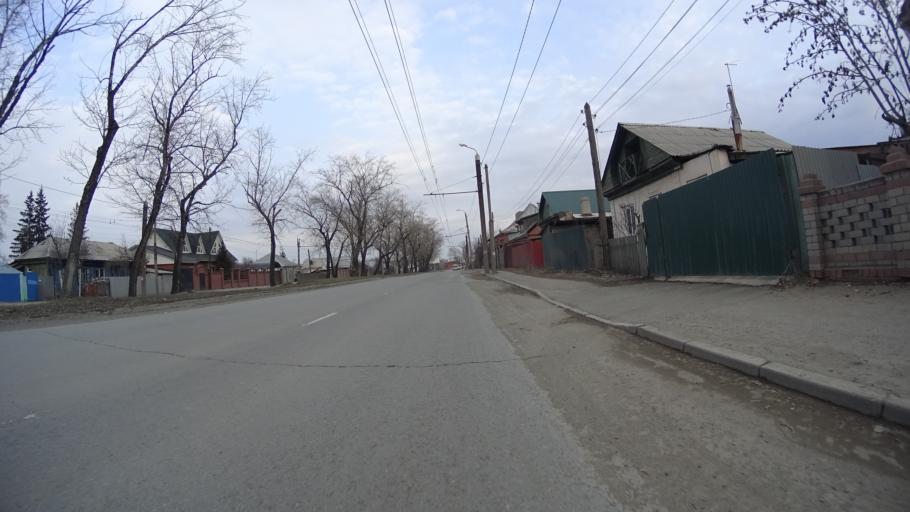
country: RU
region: Chelyabinsk
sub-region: Gorod Chelyabinsk
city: Chelyabinsk
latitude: 55.1913
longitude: 61.4722
